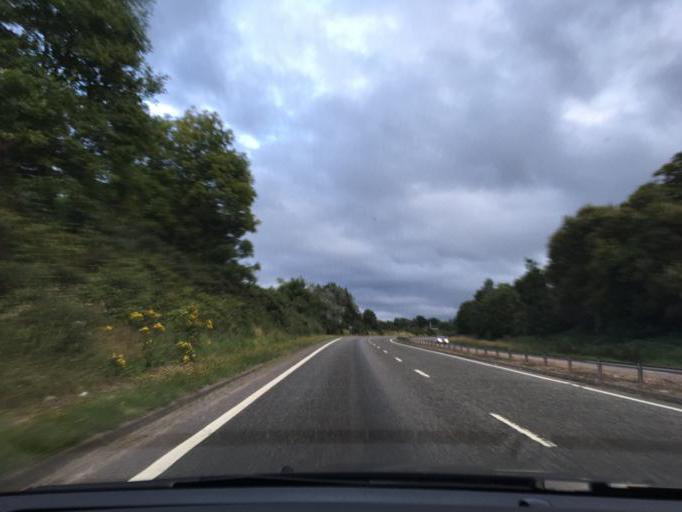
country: GB
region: Scotland
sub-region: Highland
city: Inverness
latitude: 57.4645
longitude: -4.1727
